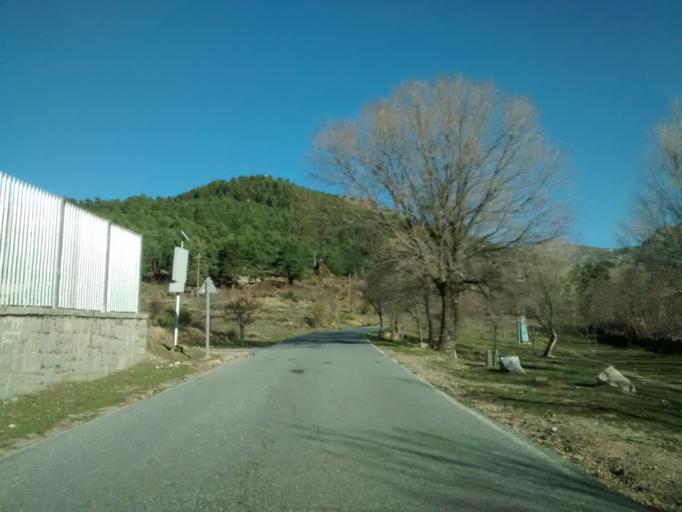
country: ES
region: Madrid
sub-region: Provincia de Madrid
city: Navacerrada
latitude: 40.7407
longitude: -4.0040
